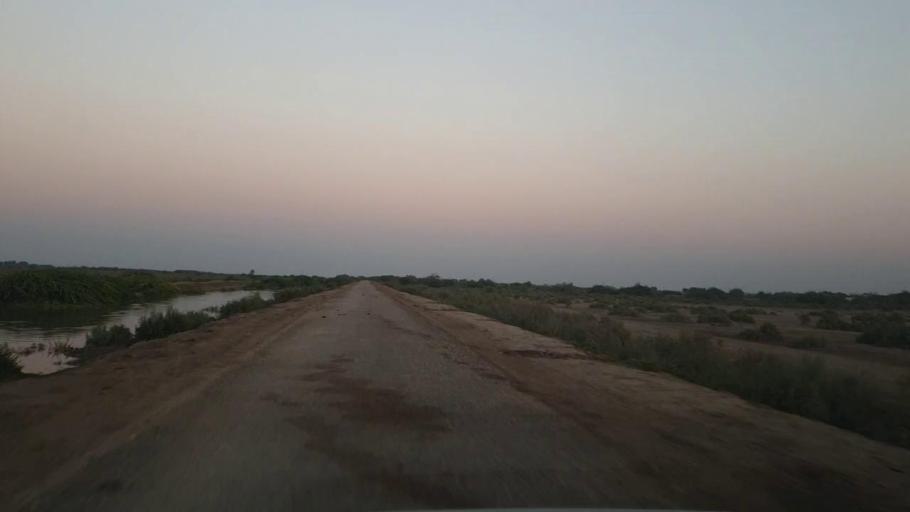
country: PK
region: Sindh
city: Mirpur Sakro
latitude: 24.3868
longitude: 67.5812
